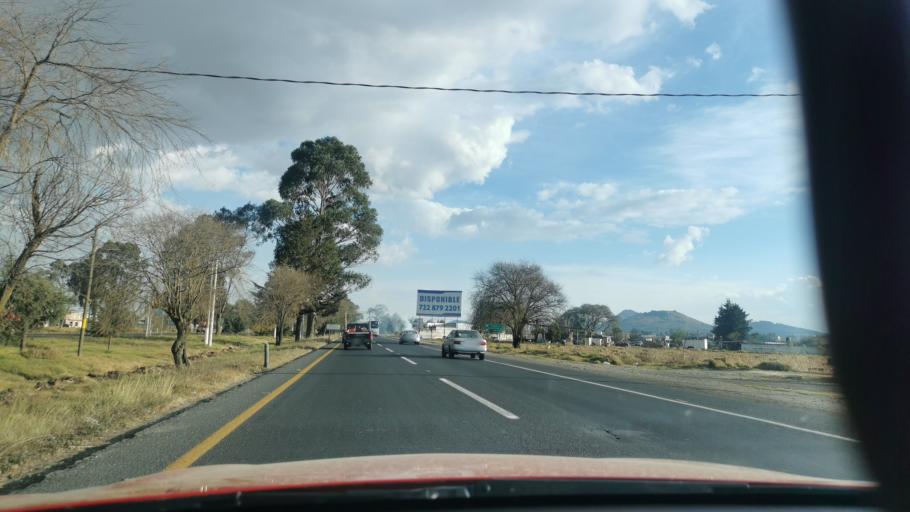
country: MX
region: Mexico
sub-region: Toluca
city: Colonia Aviacion Autopan
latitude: 19.3793
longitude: -99.7032
